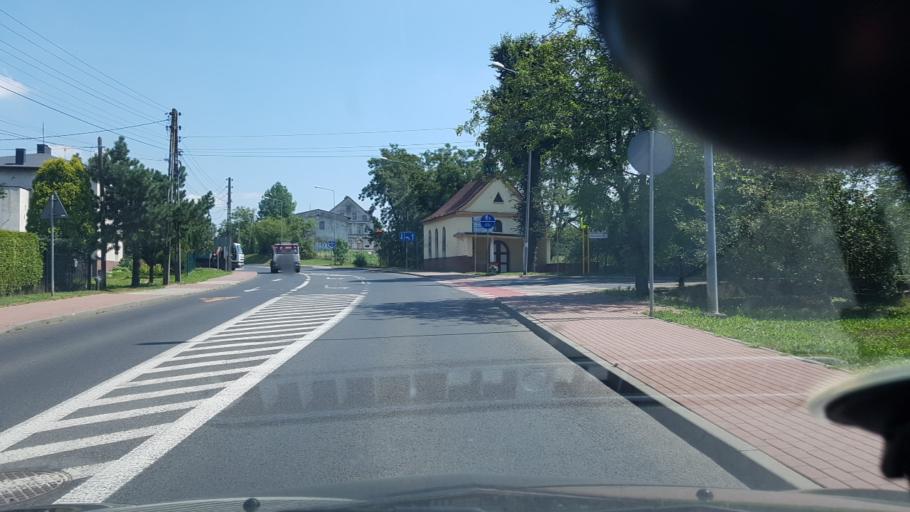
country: PL
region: Silesian Voivodeship
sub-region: Zory
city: Zory
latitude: 50.0351
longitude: 18.6544
